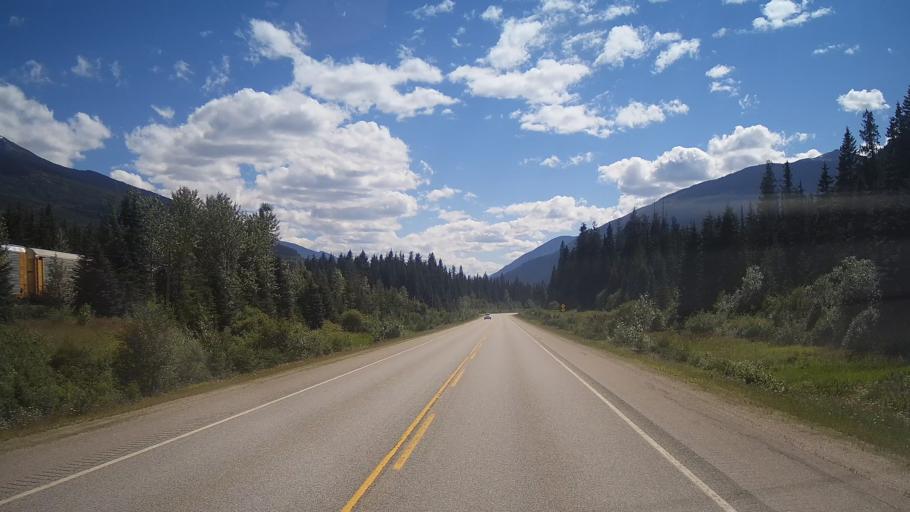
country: CA
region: Alberta
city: Jasper Park Lodge
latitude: 52.5738
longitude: -119.0990
